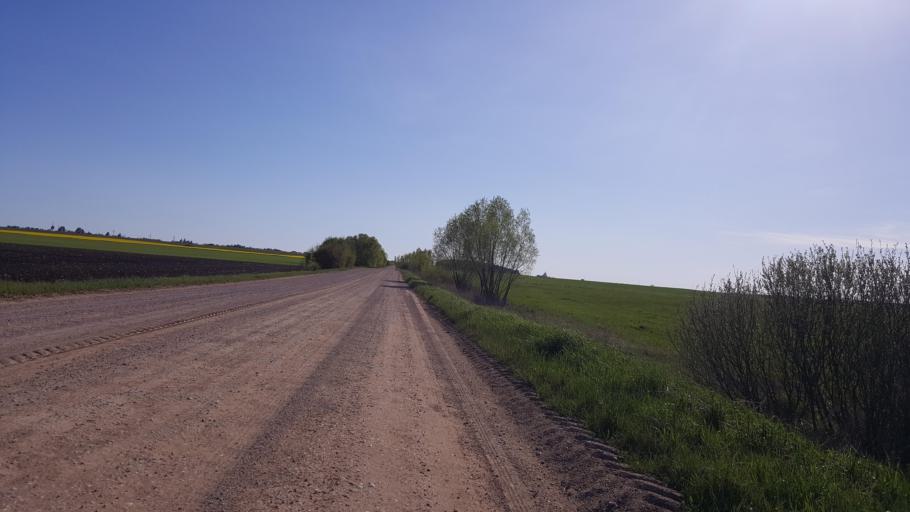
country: BY
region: Brest
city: Kamyanyets
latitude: 52.4183
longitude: 23.8670
